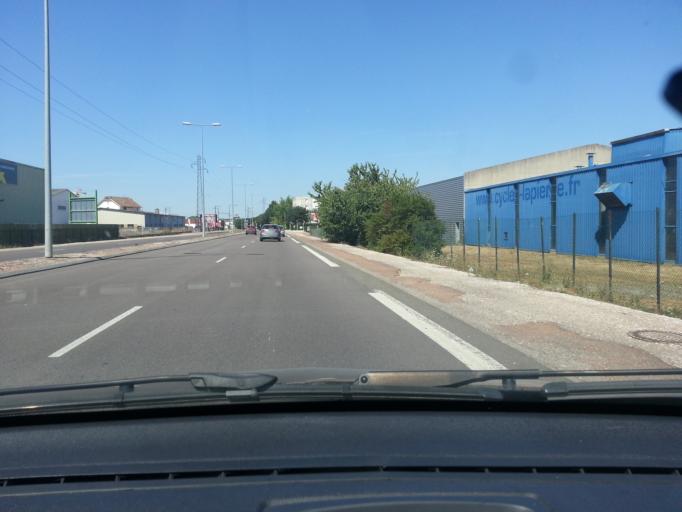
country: FR
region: Bourgogne
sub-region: Departement de la Cote-d'Or
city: Dijon
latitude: 47.2985
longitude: 5.0238
